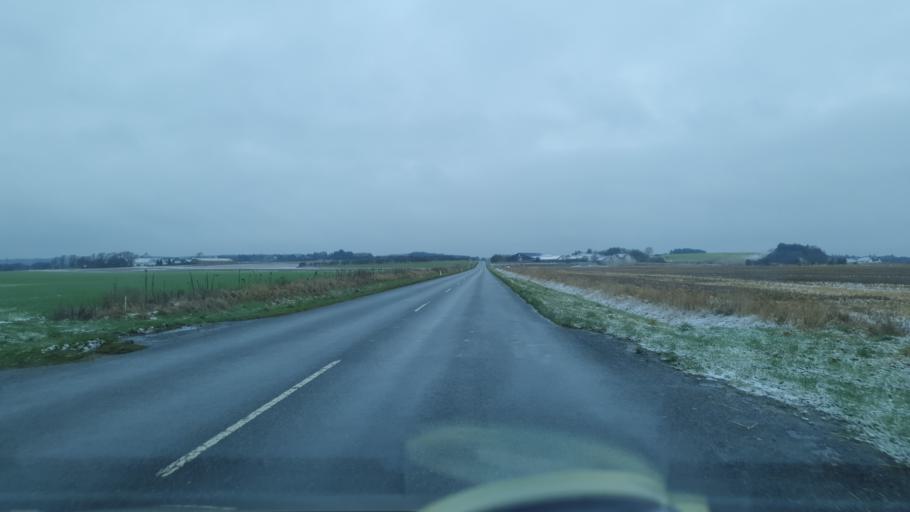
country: DK
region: North Denmark
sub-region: Jammerbugt Kommune
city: Brovst
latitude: 57.1185
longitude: 9.4973
